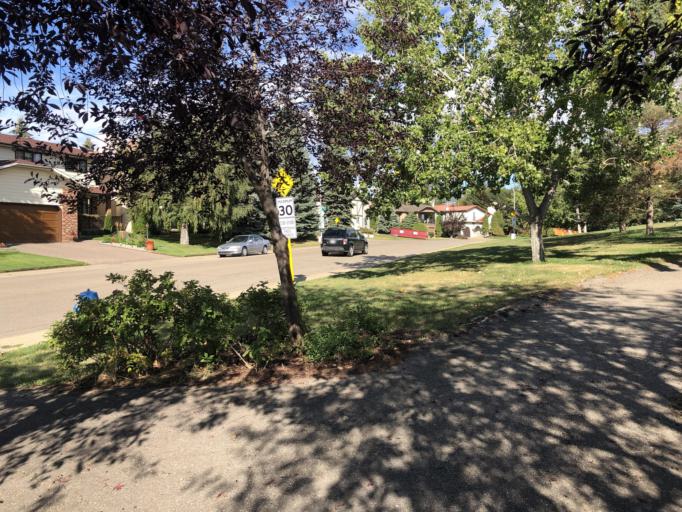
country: CA
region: Alberta
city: Edmonton
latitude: 53.4815
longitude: -113.5836
